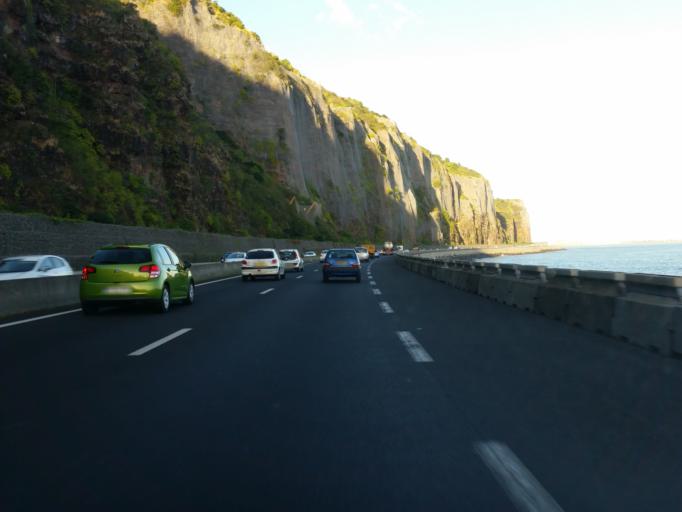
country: RE
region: Reunion
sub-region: Reunion
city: La Possession
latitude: -20.9051
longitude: 55.3641
